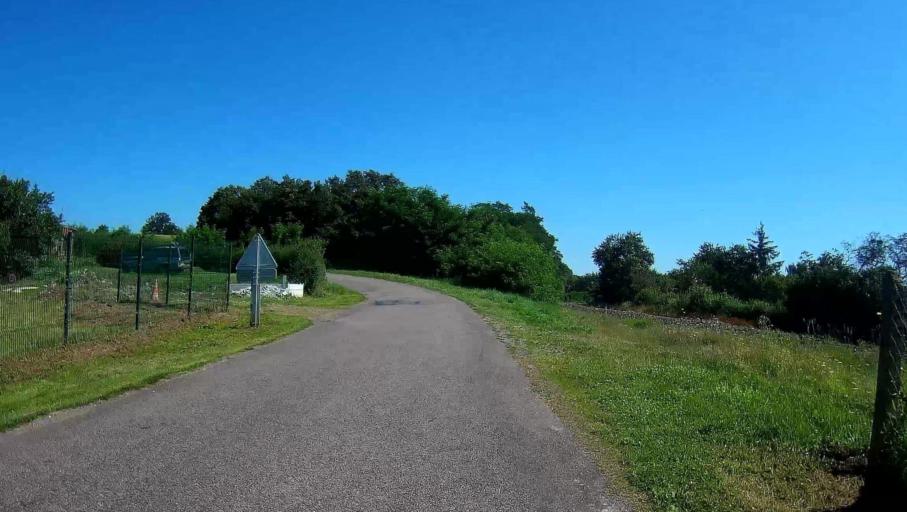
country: FR
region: Bourgogne
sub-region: Departement de Saone-et-Loire
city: Saint-Leger-sur-Dheune
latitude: 46.8258
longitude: 4.5954
